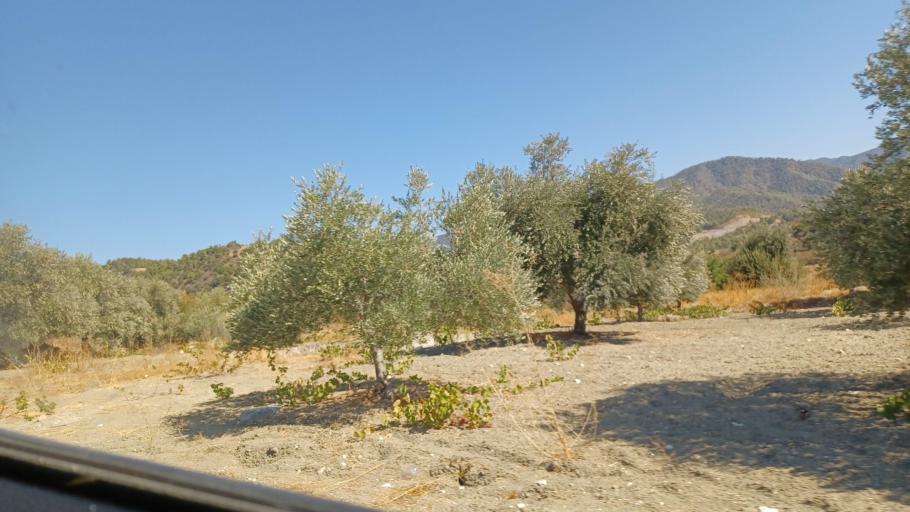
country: CY
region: Pafos
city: Mesogi
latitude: 34.9207
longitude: 32.5742
